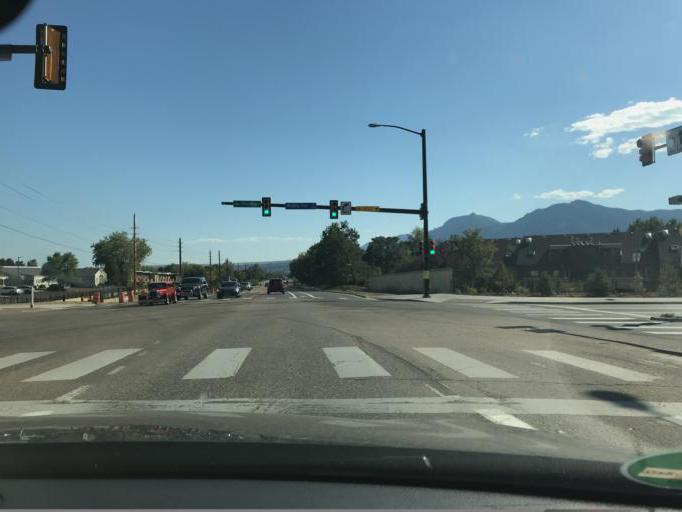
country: US
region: Colorado
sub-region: Boulder County
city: Boulder
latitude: 40.0438
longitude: -105.2586
